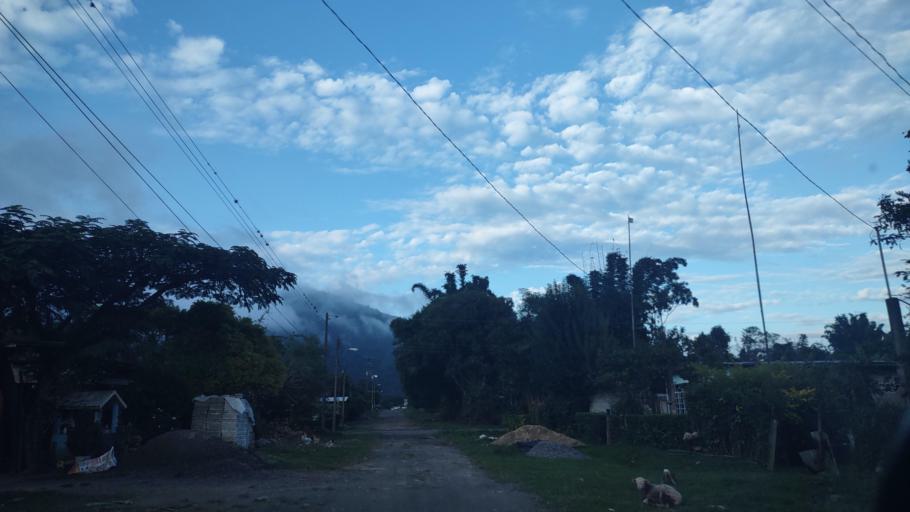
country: MX
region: Veracruz
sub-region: Ixtaczoquitlan
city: Buenavista
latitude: 18.9204
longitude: -97.0451
